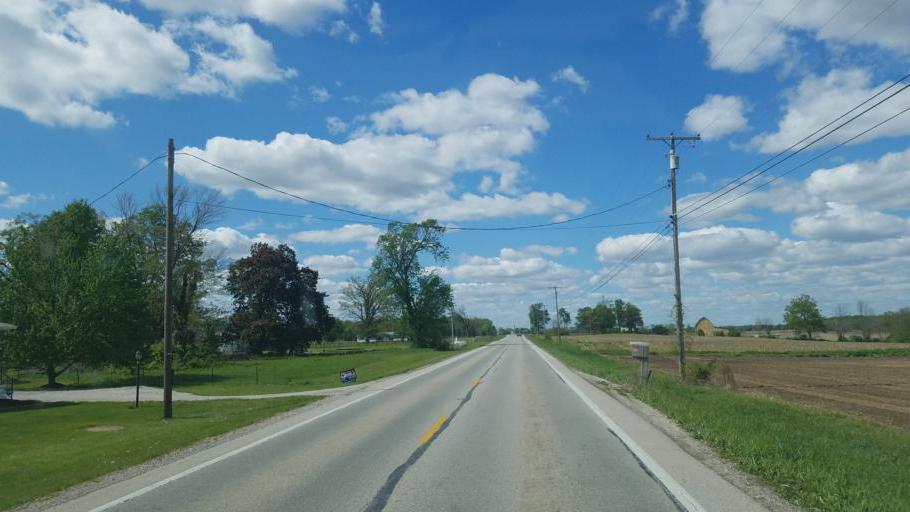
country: US
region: Ohio
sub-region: Marion County
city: Marion
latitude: 40.4954
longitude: -83.0906
